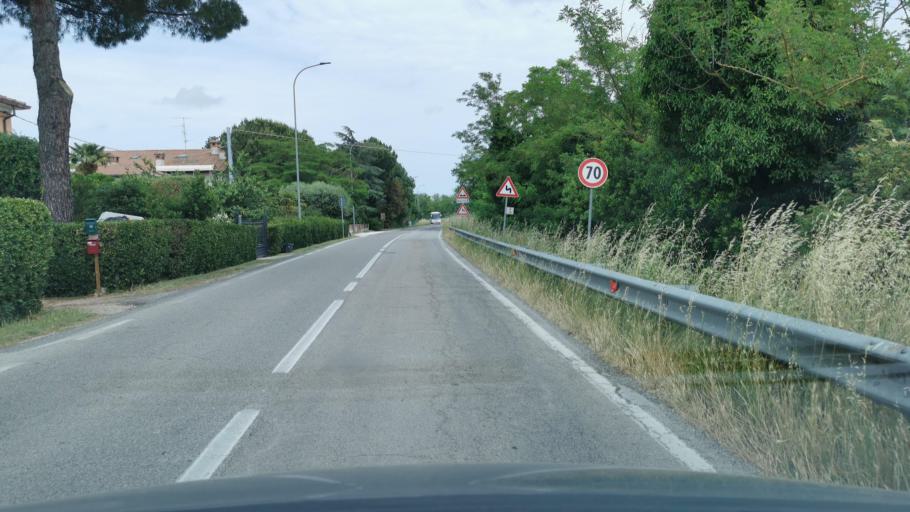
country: IT
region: Emilia-Romagna
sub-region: Provincia di Ravenna
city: Sant'Alberto
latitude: 44.5449
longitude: 12.2079
